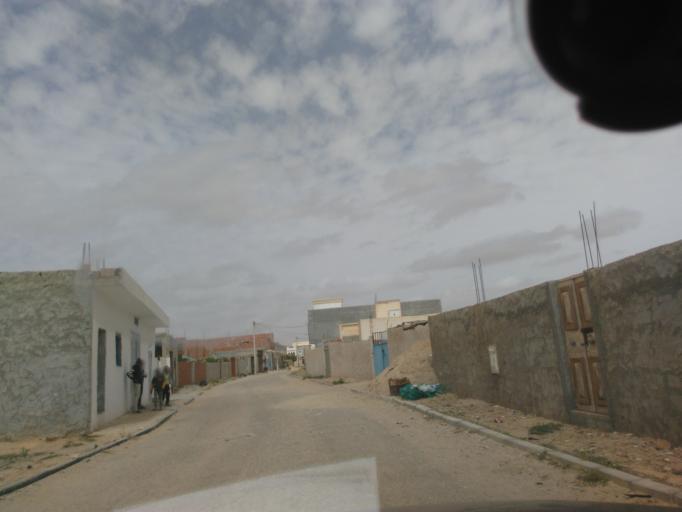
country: TN
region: Tataouine
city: Tataouine
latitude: 32.9473
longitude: 10.4720
